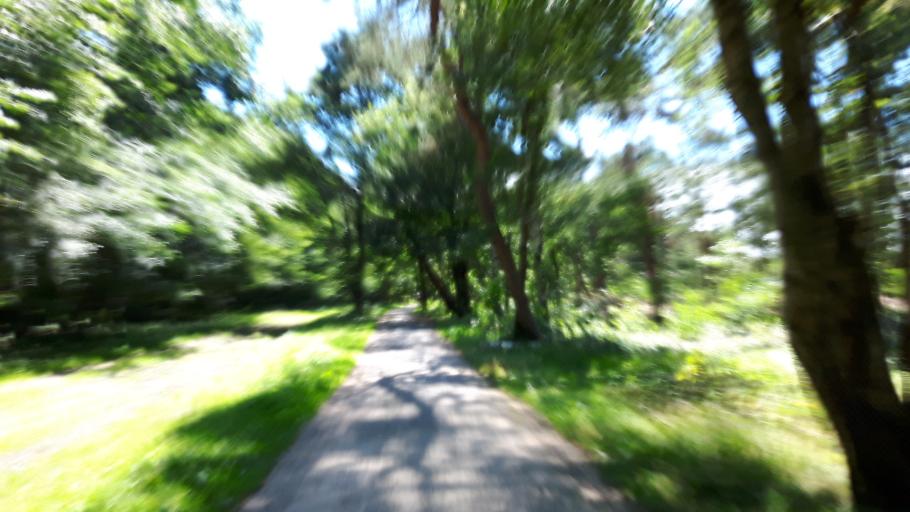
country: NL
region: North Holland
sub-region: Gemeente Wijdemeren
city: Nieuw-Loosdrecht
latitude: 52.1972
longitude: 5.1566
